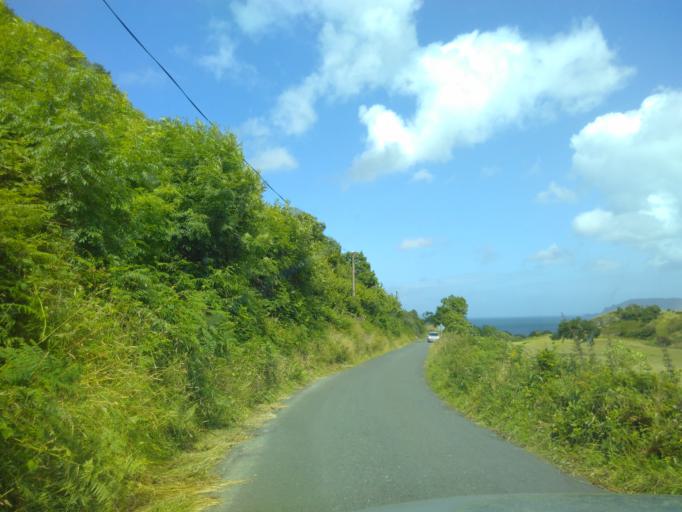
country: IE
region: Ulster
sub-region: County Donegal
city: Ramelton
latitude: 55.2257
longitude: -7.6234
